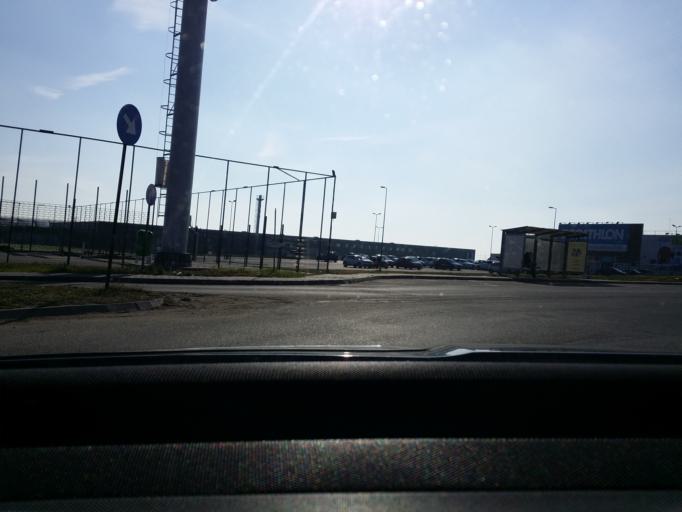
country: RO
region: Prahova
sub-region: Comuna Paulesti
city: Paulesti
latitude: 44.9648
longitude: 25.9699
